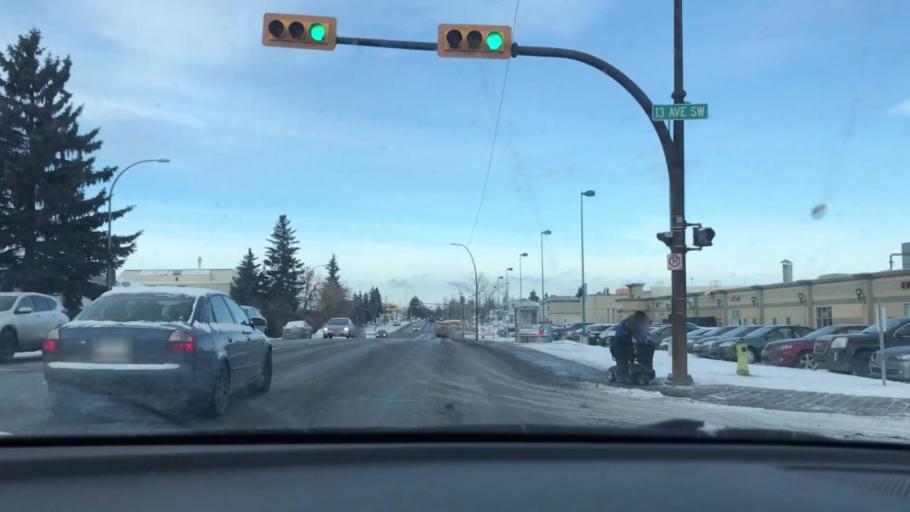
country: CA
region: Alberta
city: Calgary
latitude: 51.0415
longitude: -114.1411
